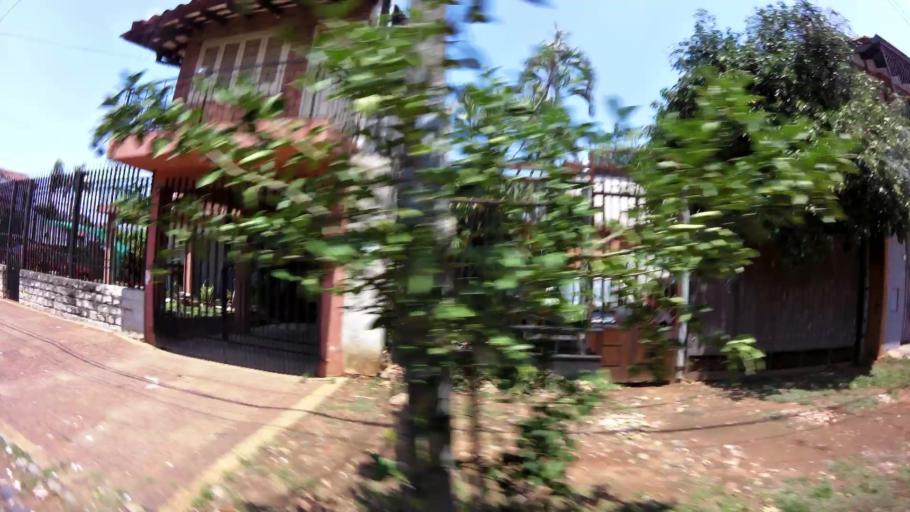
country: PY
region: Asuncion
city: Asuncion
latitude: -25.2932
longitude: -57.6480
